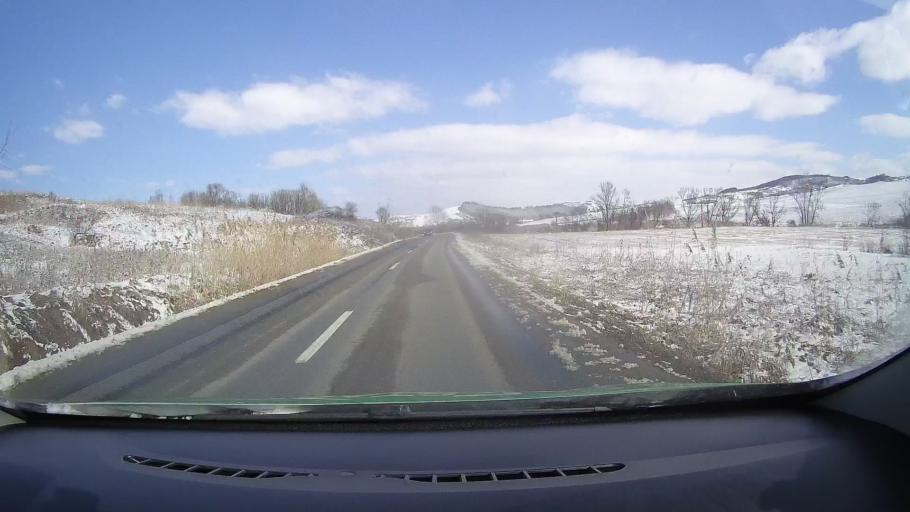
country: RO
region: Sibiu
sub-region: Comuna Altina
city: Altina
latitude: 45.9809
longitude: 24.4713
